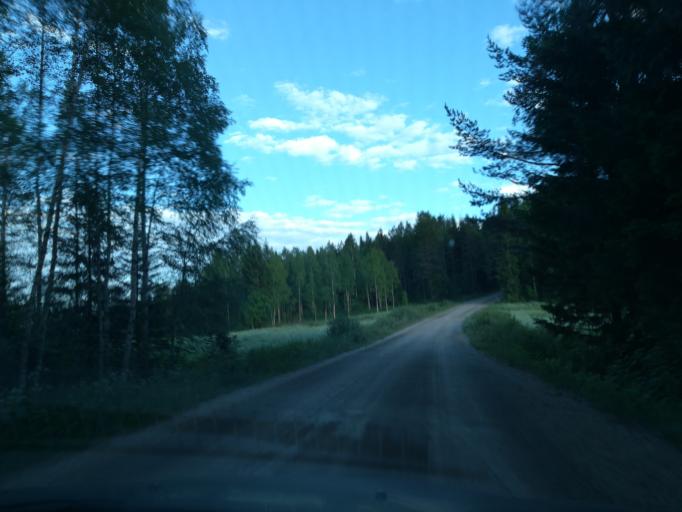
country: FI
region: Southern Savonia
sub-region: Mikkeli
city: Puumala
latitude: 61.6017
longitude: 28.1182
